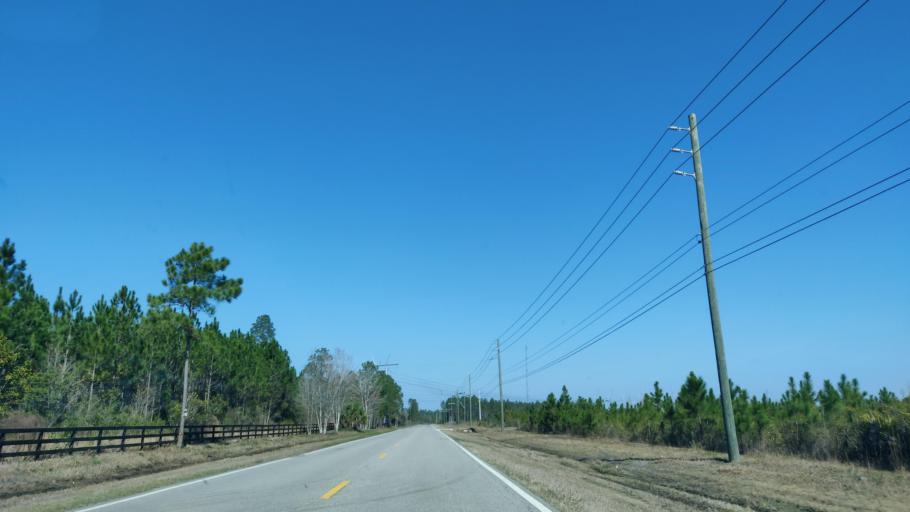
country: US
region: Florida
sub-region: Duval County
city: Baldwin
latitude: 30.2584
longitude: -81.9518
